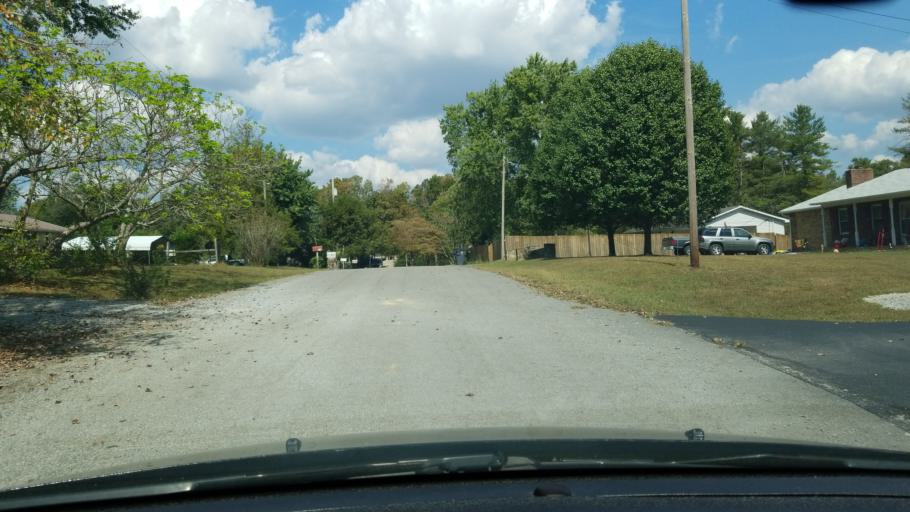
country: US
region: Tennessee
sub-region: Cumberland County
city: Crossville
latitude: 35.9602
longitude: -85.0693
